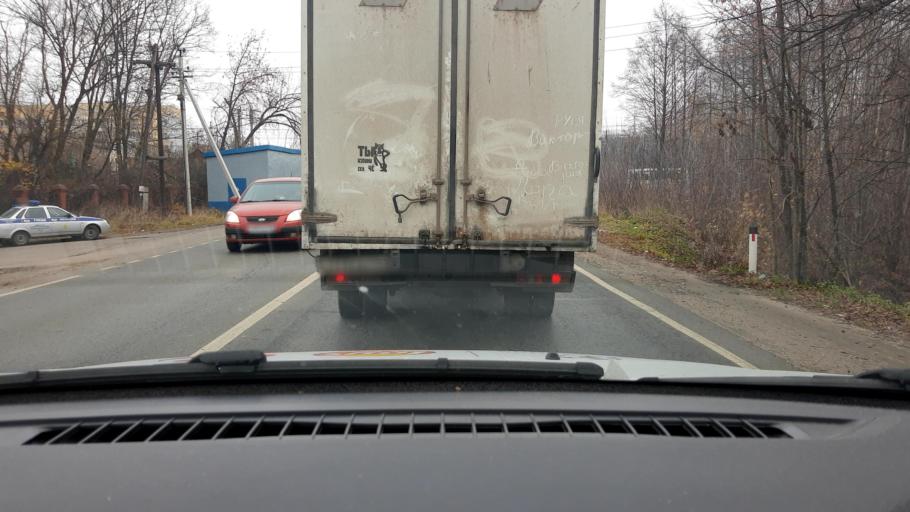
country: RU
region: Nizjnij Novgorod
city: Novaya Balakhna
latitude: 56.5165
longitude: 43.5812
